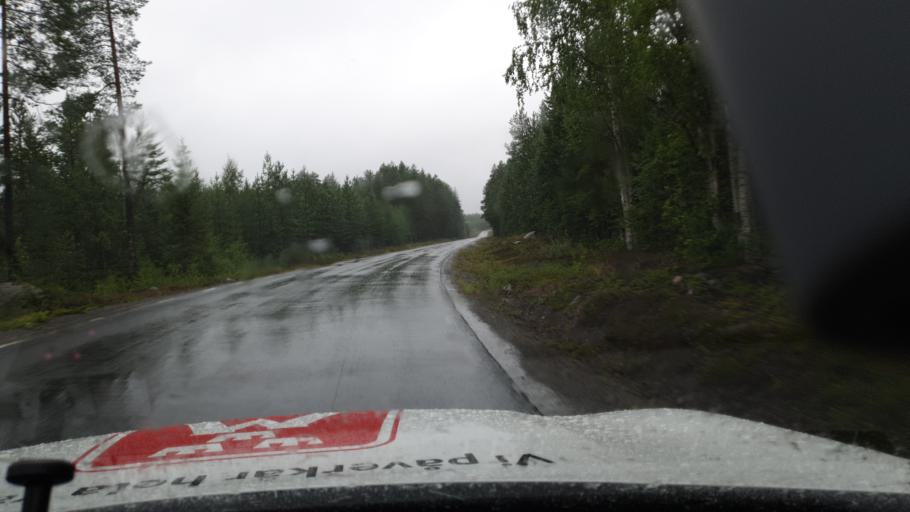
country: SE
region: Vaesterbotten
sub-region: Skelleftea Kommun
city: Burea
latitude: 64.6092
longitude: 21.1675
